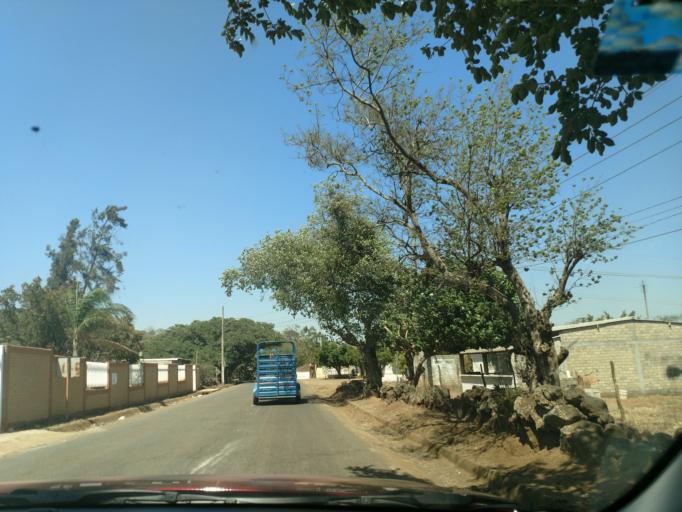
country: MX
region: Nayarit
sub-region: Tepic
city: La Corregidora
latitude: 21.5047
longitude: -104.7106
